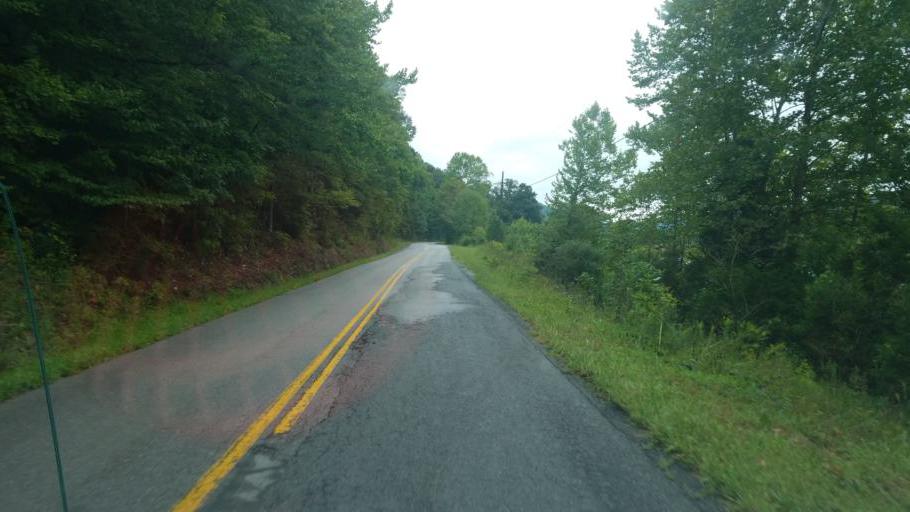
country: US
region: Kentucky
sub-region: Fleming County
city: Flemingsburg
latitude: 38.3764
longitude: -83.5410
